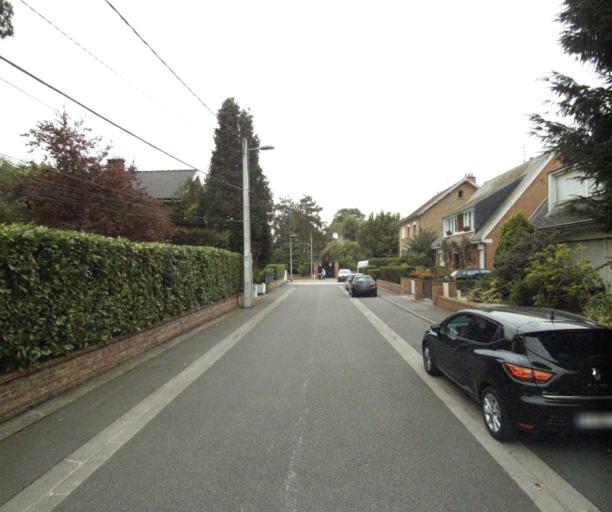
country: FR
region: Nord-Pas-de-Calais
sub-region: Departement du Nord
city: Saint-Andre-lez-Lille
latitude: 50.6572
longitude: 3.0451
